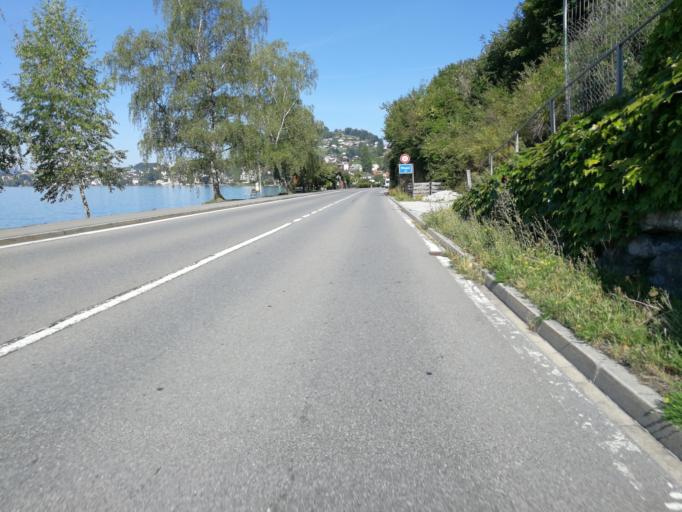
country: CH
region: Lucerne
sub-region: Lucerne-Land District
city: Weggis
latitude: 47.0271
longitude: 8.4496
